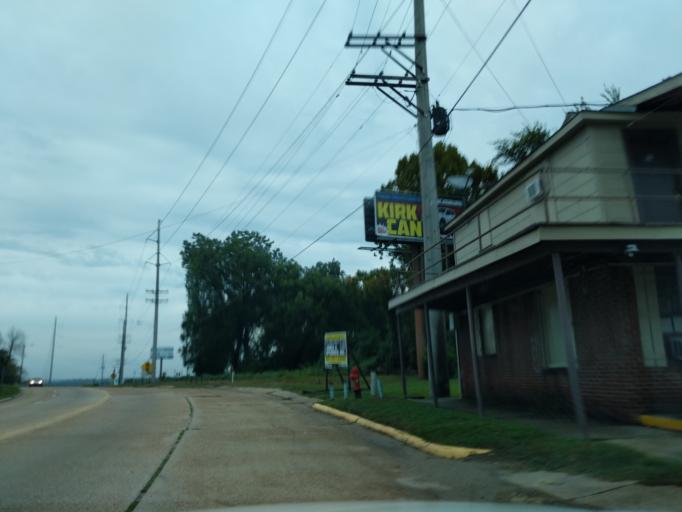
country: US
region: Mississippi
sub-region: Warren County
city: Vicksburg
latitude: 32.3204
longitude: -90.8963
